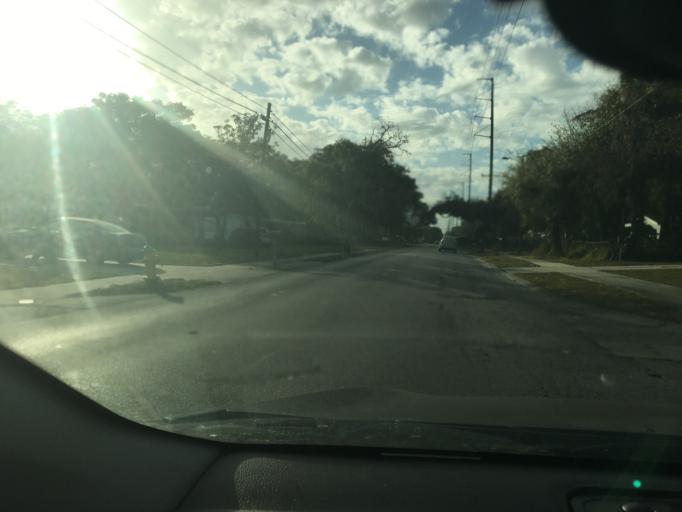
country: US
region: Florida
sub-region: Hillsborough County
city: University
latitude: 28.0436
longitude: -82.4373
